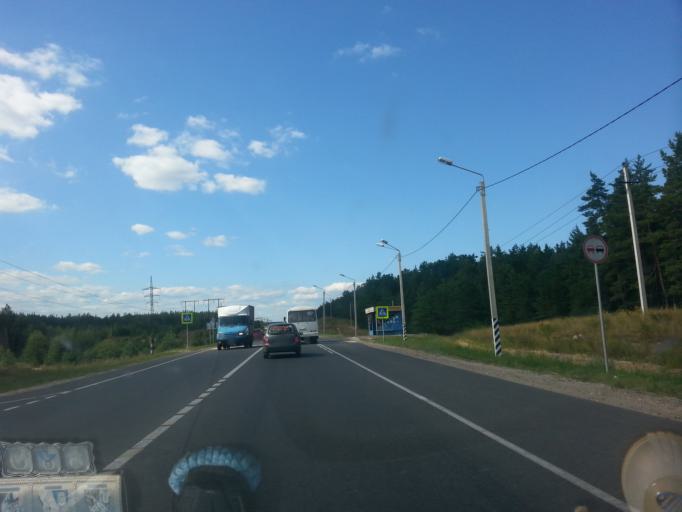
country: RU
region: Nizjnij Novgorod
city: Lukino
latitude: 56.3911
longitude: 43.6924
